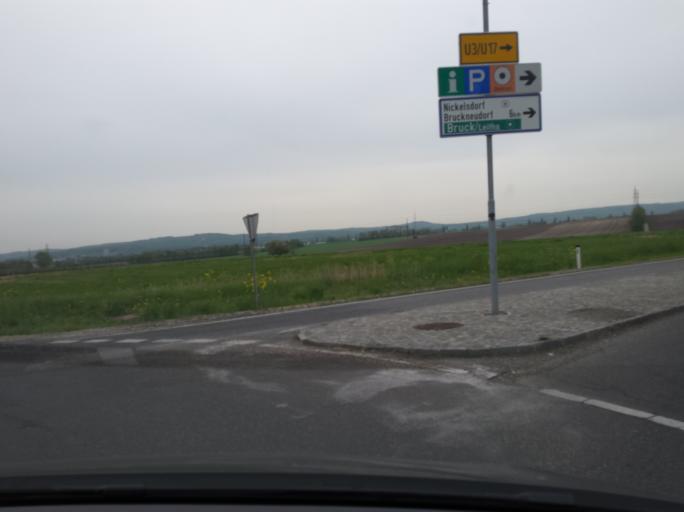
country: AT
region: Lower Austria
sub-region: Politischer Bezirk Bruck an der Leitha
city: Bruck an der Leitha
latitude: 48.0406
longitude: 16.7518
